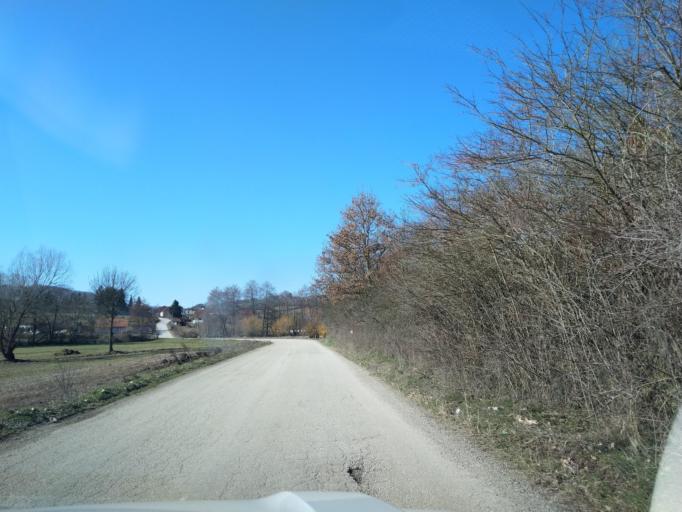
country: RS
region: Central Serbia
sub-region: Zlatiborski Okrug
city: Kosjeric
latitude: 43.9377
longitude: 19.8797
